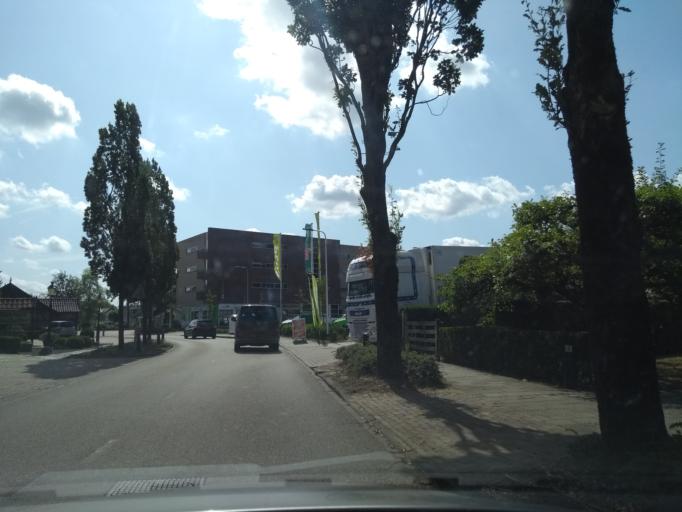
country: DE
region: Lower Saxony
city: Nordhorn
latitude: 52.3731
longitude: 7.0016
